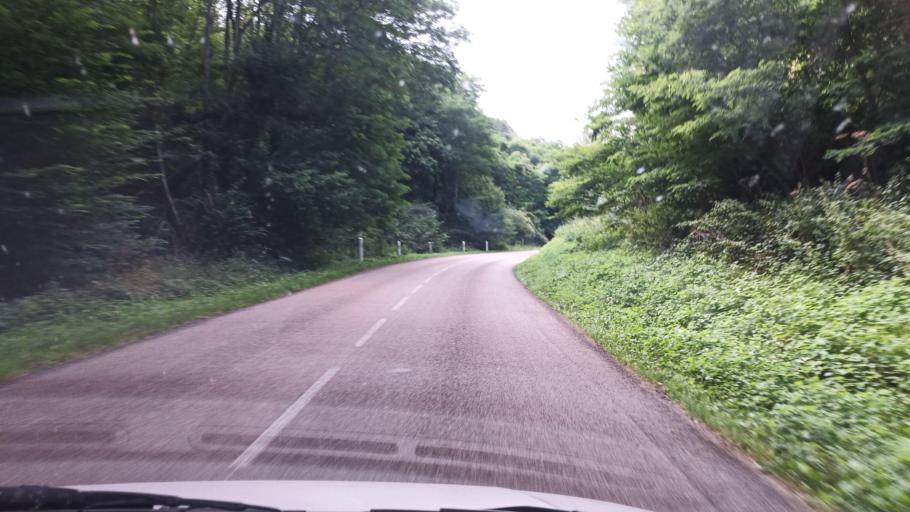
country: FR
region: Bourgogne
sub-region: Departement de l'Yonne
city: Villeneuve-sur-Yonne
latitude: 48.0714
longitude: 3.2662
